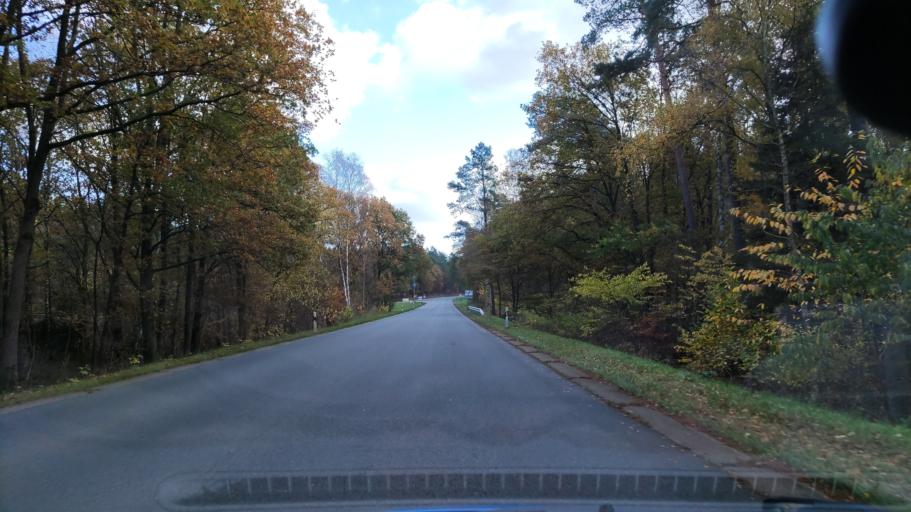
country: DE
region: Lower Saxony
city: Munster
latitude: 53.0135
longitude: 10.0958
